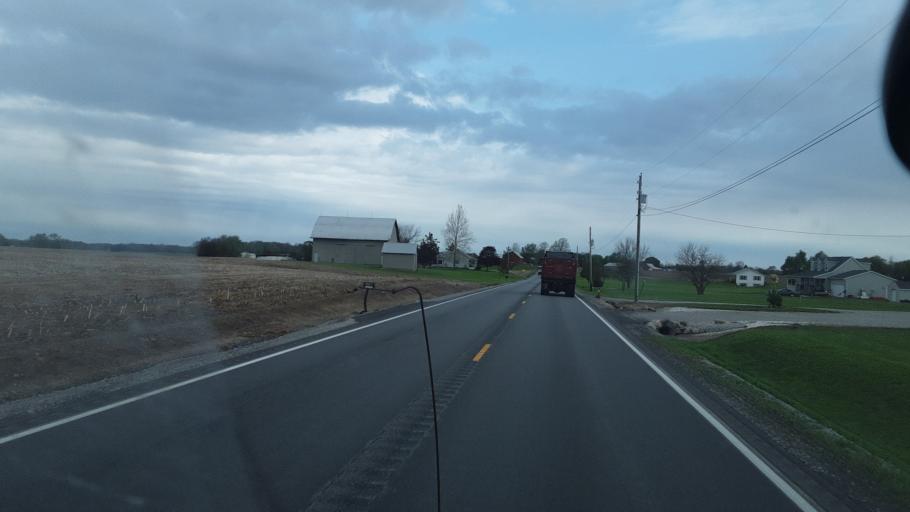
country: US
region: Indiana
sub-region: Whitley County
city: Tri-Lakes
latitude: 41.3113
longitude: -85.4631
